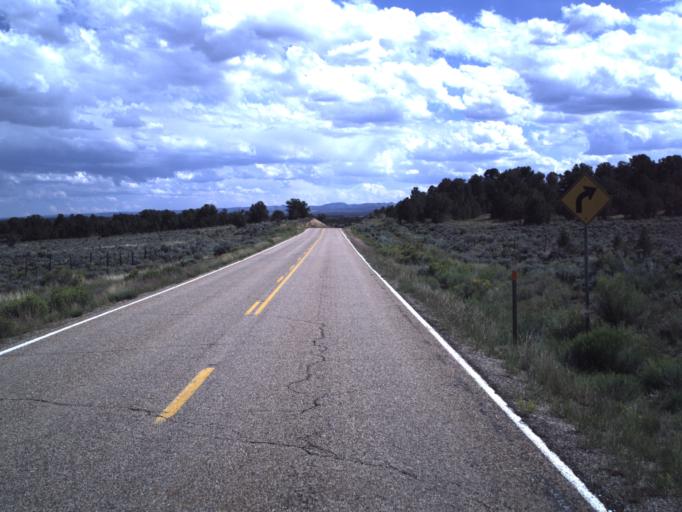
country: US
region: Utah
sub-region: Duchesne County
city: Duchesne
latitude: 40.2963
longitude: -110.6955
